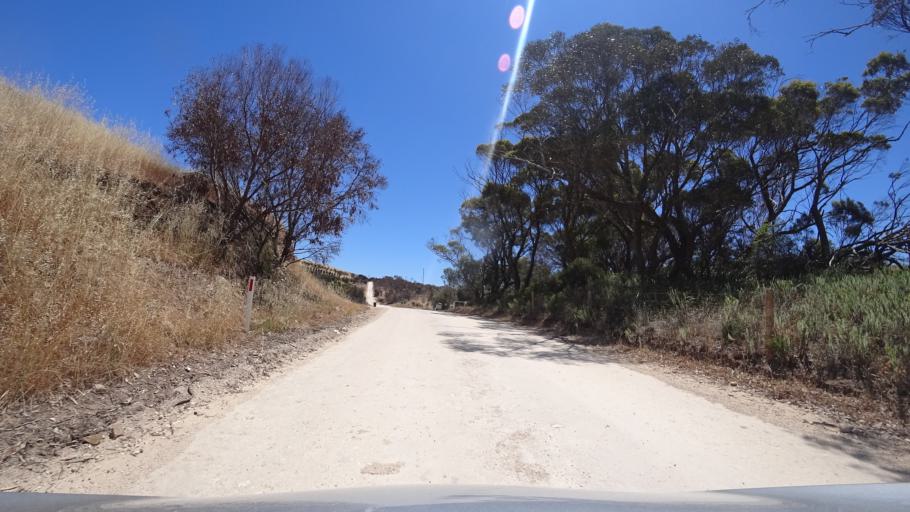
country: AU
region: South Australia
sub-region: Kangaroo Island
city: Kingscote
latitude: -35.6697
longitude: 137.0738
